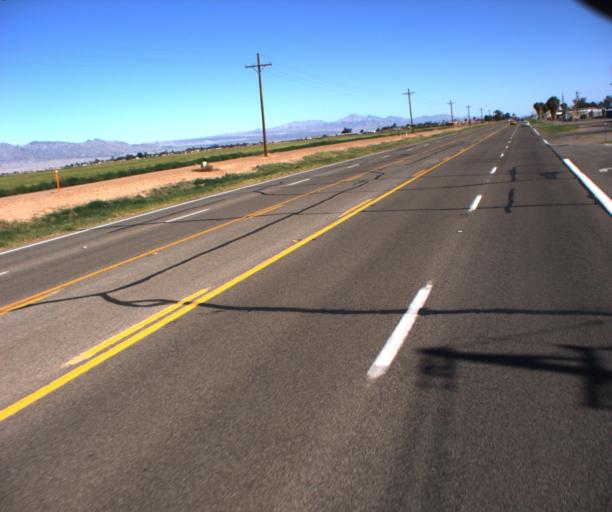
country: US
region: Arizona
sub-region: Mohave County
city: Willow Valley
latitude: 34.8974
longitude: -114.5978
